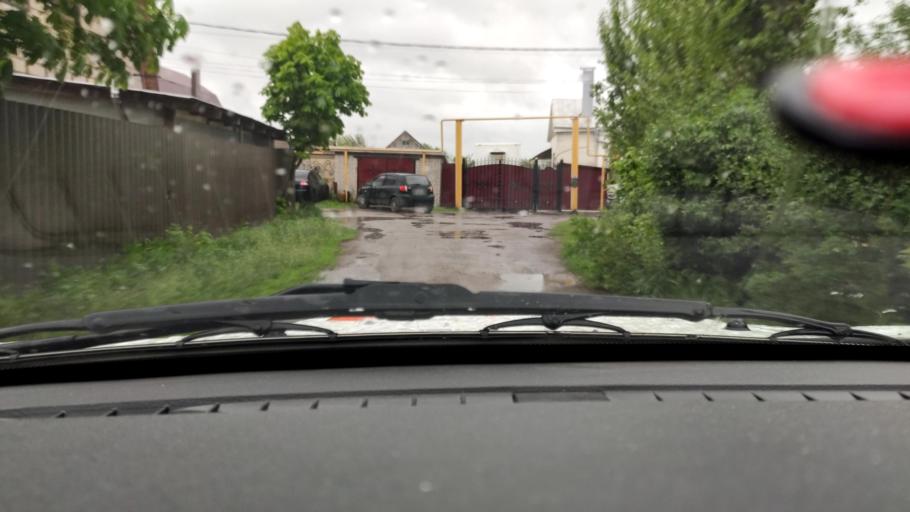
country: RU
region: Voronezj
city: Novaya Usman'
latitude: 51.6327
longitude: 39.3946
